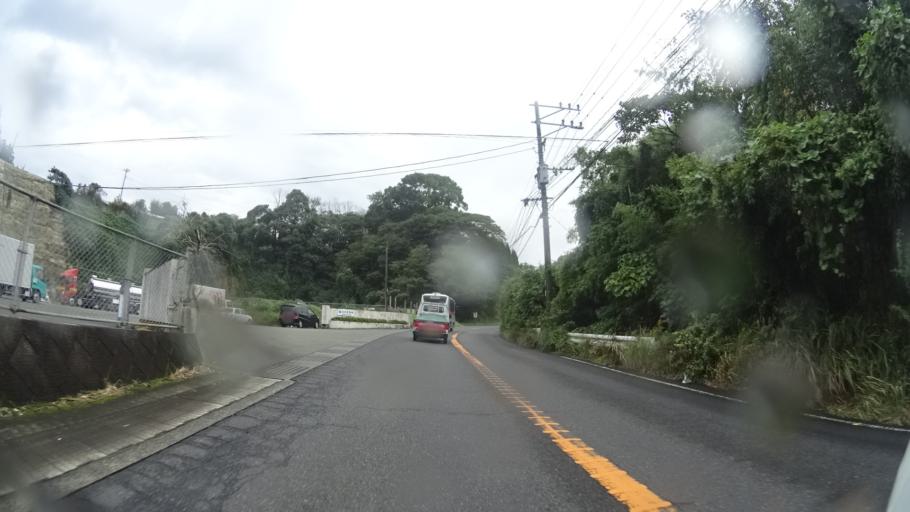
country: JP
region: Kagoshima
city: Kajiki
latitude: 31.7738
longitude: 130.6693
